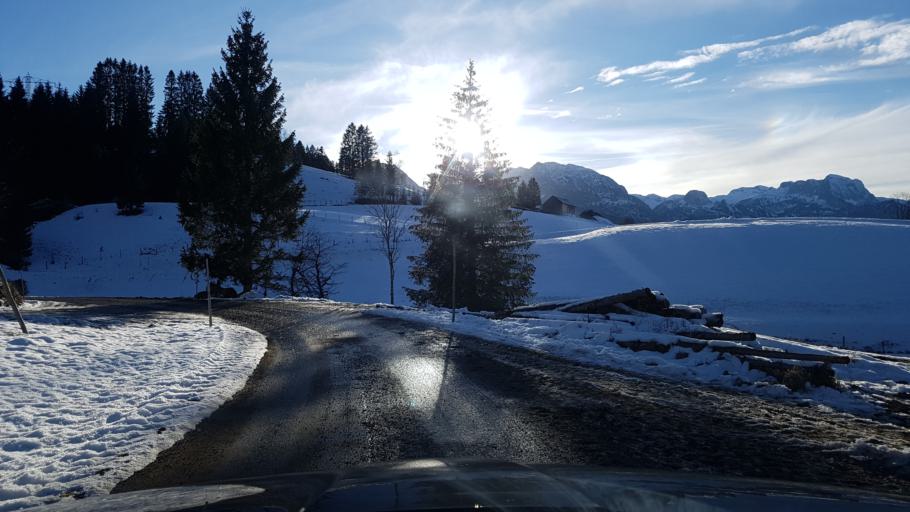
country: AT
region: Salzburg
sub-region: Politischer Bezirk Hallein
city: Abtenau
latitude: 47.5745
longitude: 13.4137
